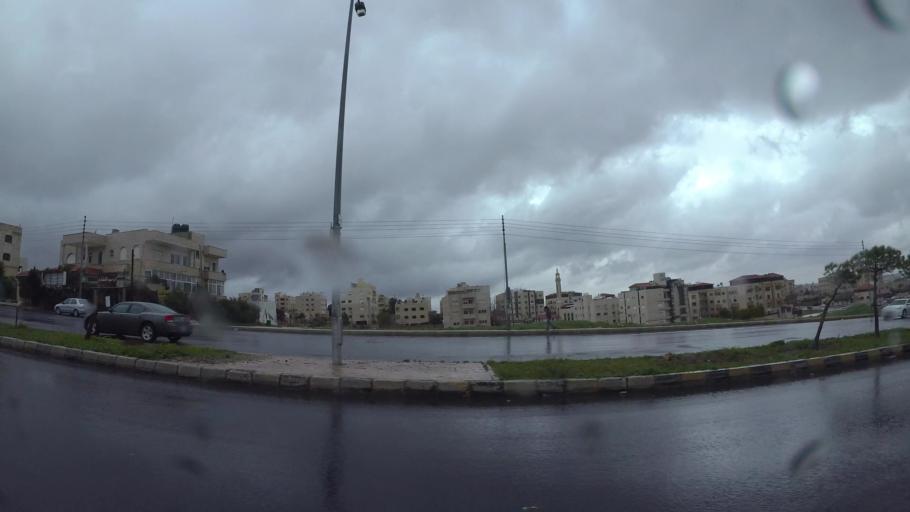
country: JO
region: Amman
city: Al Jubayhah
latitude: 32.0443
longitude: 35.8978
